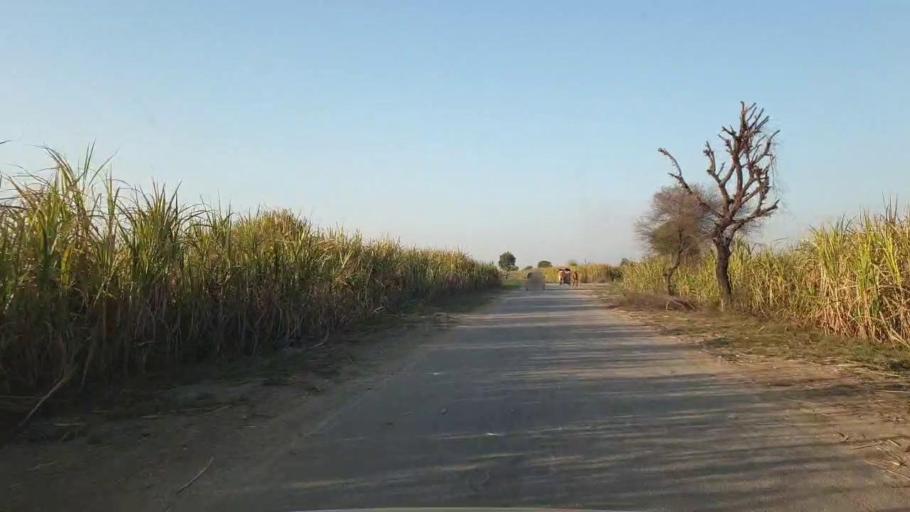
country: PK
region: Sindh
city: Chambar
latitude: 25.3612
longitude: 68.7401
